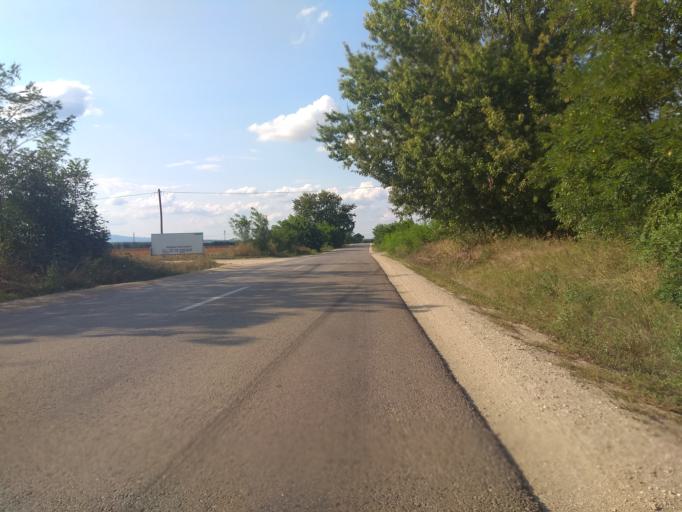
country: HU
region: Borsod-Abauj-Zemplen
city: Hejobaba
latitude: 47.8982
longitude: 20.8916
